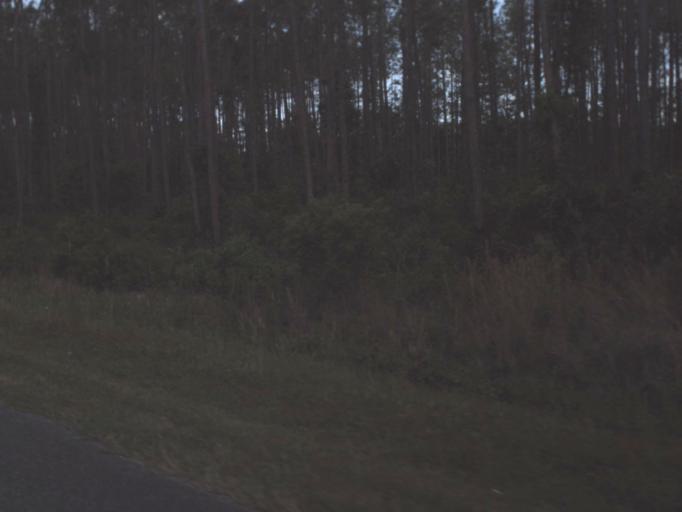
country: US
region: Florida
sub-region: Marion County
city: Silver Springs Shores
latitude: 29.2129
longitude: -81.9603
